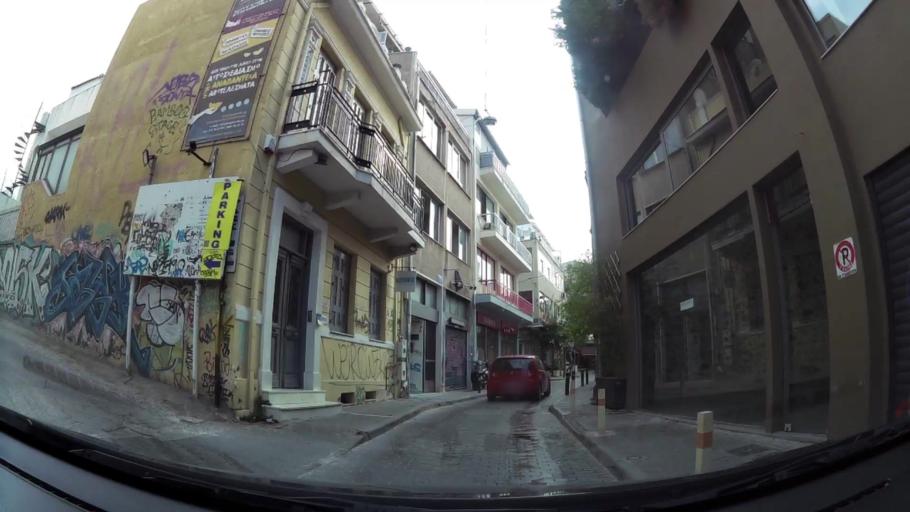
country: GR
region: Attica
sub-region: Nomarchia Athinas
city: Athens
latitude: 37.9784
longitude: 23.7230
